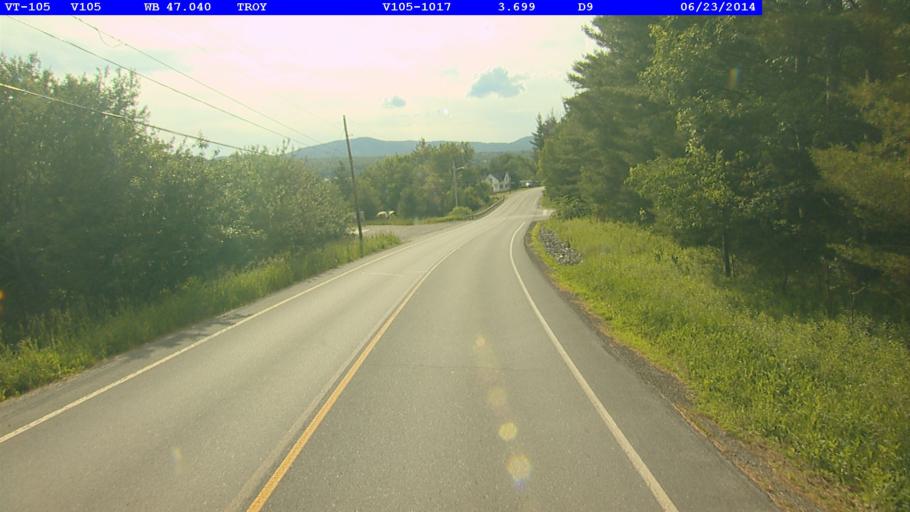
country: US
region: Vermont
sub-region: Orleans County
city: Newport
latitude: 44.9916
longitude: -72.3839
